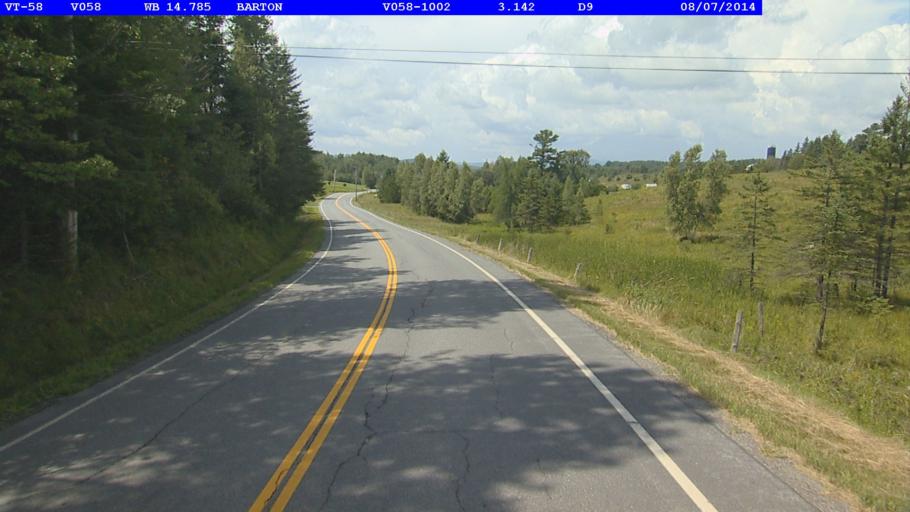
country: US
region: Vermont
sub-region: Orleans County
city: Newport
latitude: 44.8050
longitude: -72.1552
